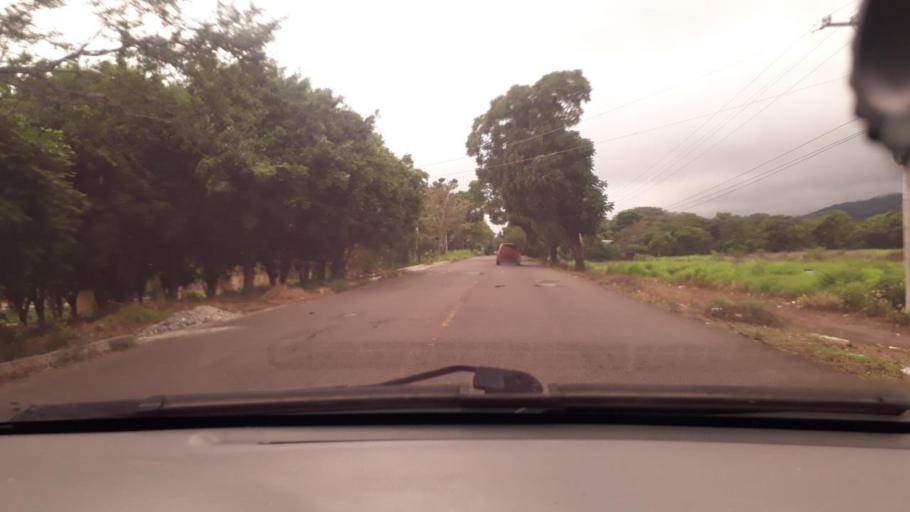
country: GT
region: Jutiapa
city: Jalpatagua
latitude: 14.1487
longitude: -90.0356
